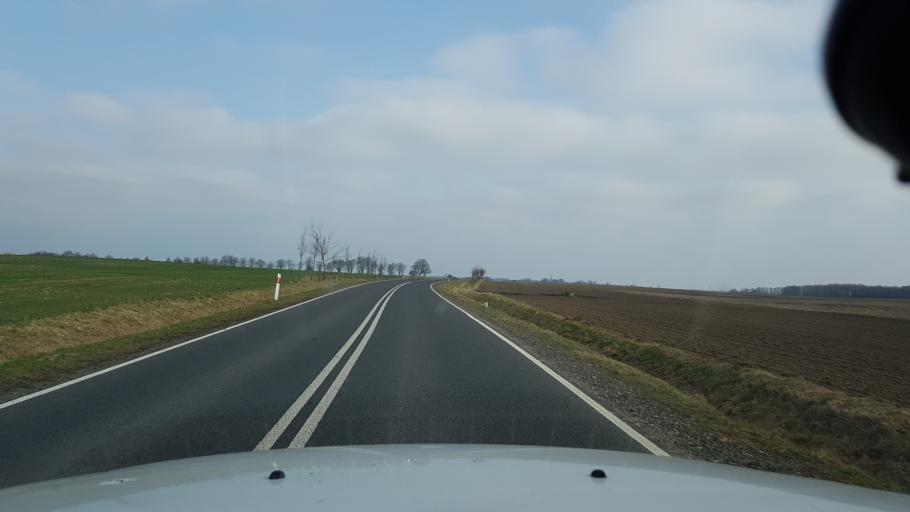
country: PL
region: West Pomeranian Voivodeship
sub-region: Powiat koszalinski
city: Sianow
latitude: 54.2755
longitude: 16.2699
